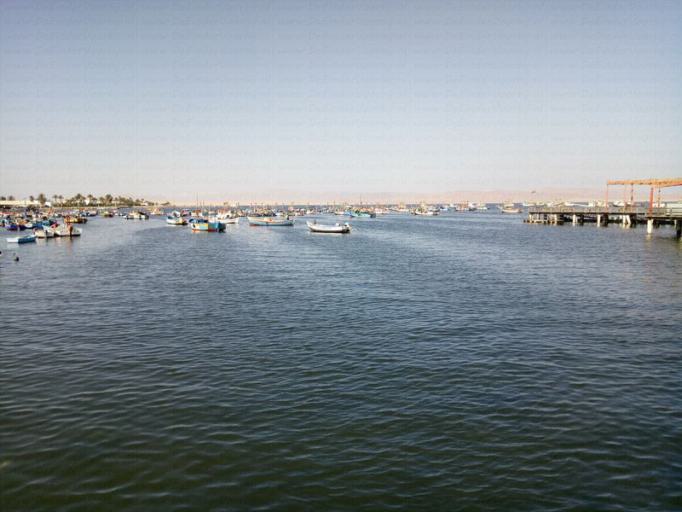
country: PE
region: Ica
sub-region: Provincia de Pisco
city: Paracas
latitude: -13.8305
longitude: -76.2476
